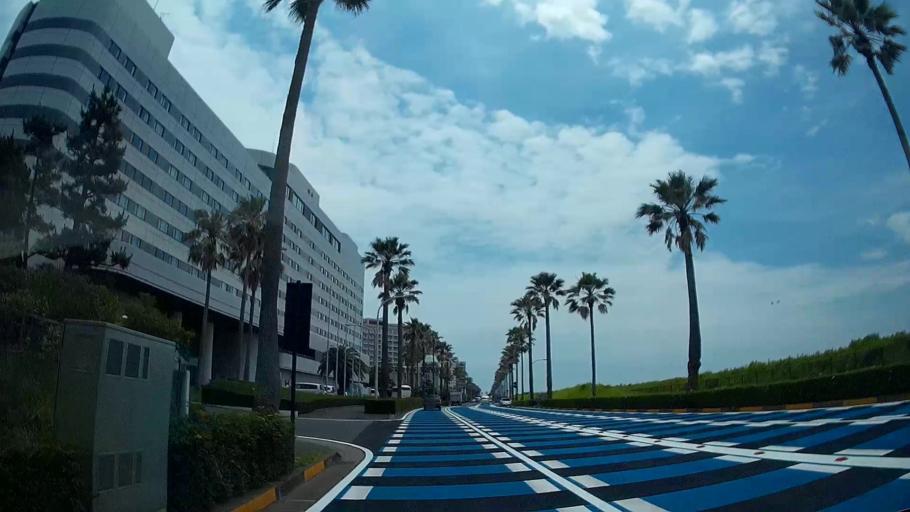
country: JP
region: Tokyo
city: Urayasu
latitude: 35.6326
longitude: 139.8732
